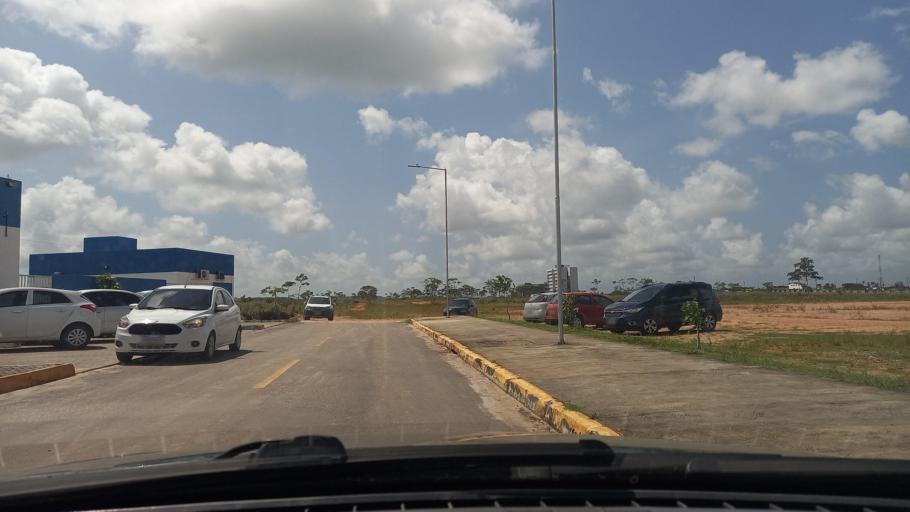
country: BR
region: Pernambuco
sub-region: Goiana
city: Goiana
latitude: -7.5543
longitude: -35.0207
